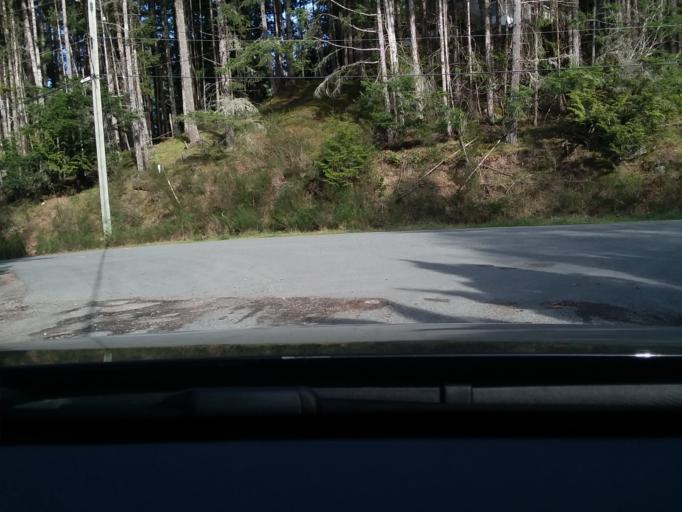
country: CA
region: British Columbia
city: North Saanich
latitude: 48.7708
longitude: -123.2936
